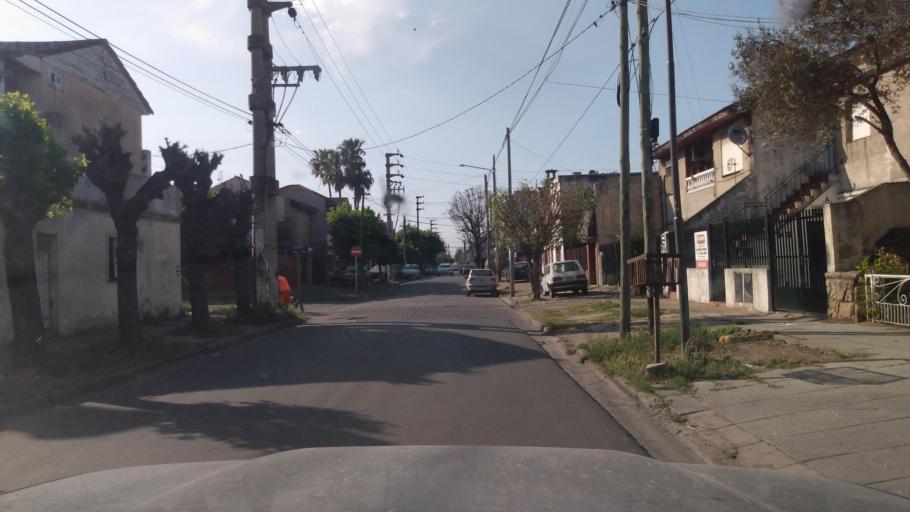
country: AR
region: Buenos Aires
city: San Justo
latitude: -34.6787
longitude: -58.5699
